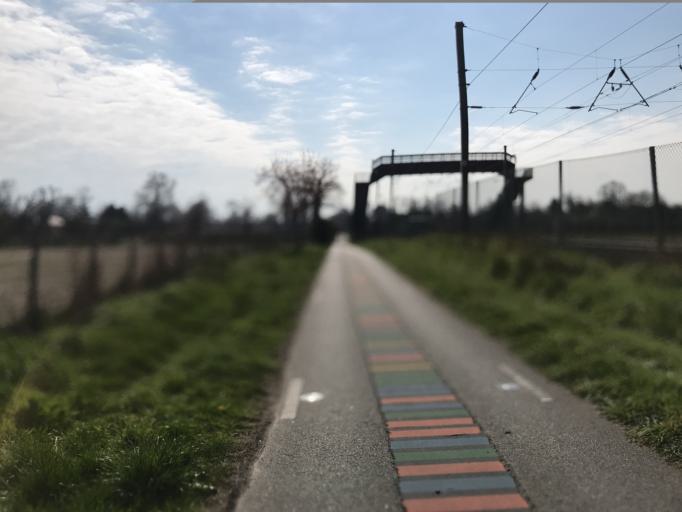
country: GB
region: England
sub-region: Cambridgeshire
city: Cambridge
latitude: 52.1579
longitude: 0.1349
